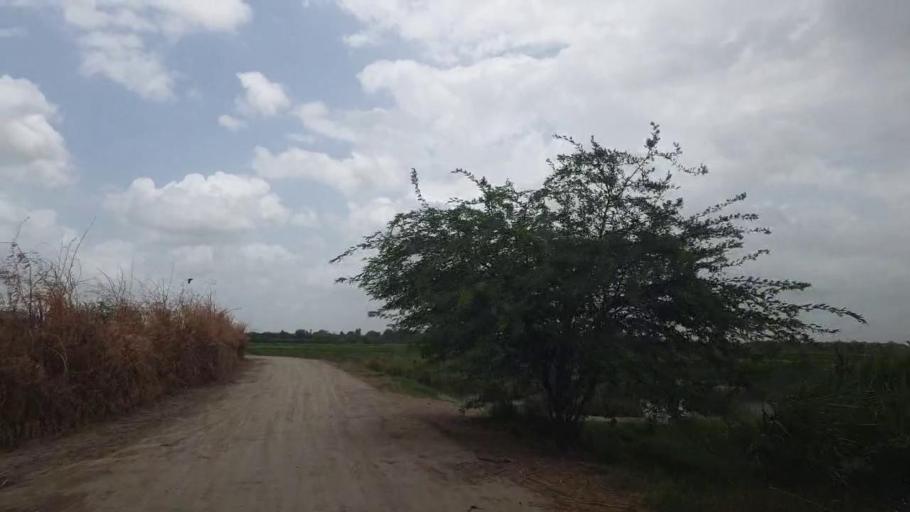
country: PK
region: Sindh
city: Badin
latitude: 24.6498
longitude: 68.9208
